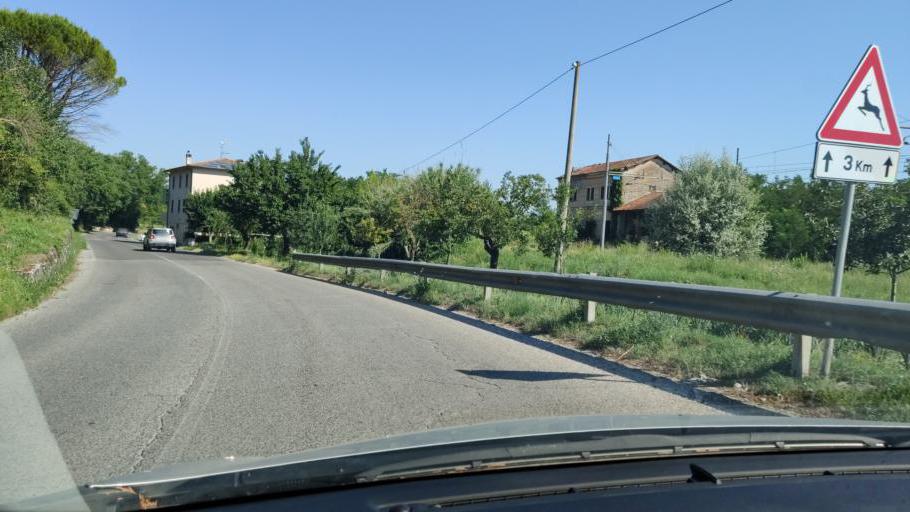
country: IT
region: Umbria
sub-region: Provincia di Perugia
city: Todi
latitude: 42.7910
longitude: 12.4170
